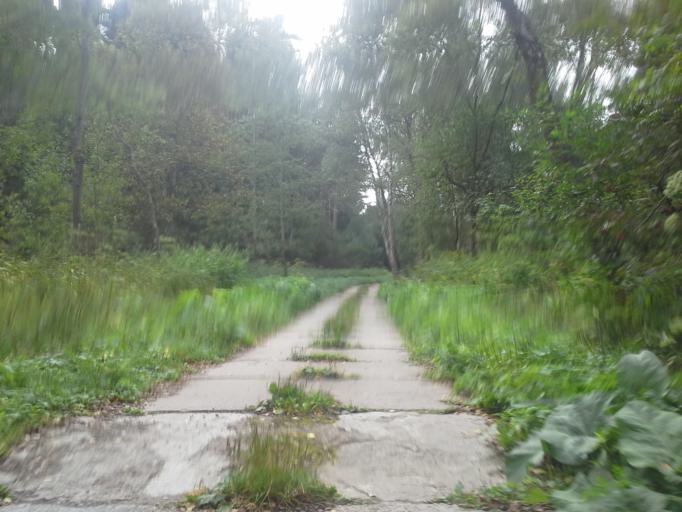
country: RU
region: Moskovskaya
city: Vatutinki
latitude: 55.5250
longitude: 37.3390
